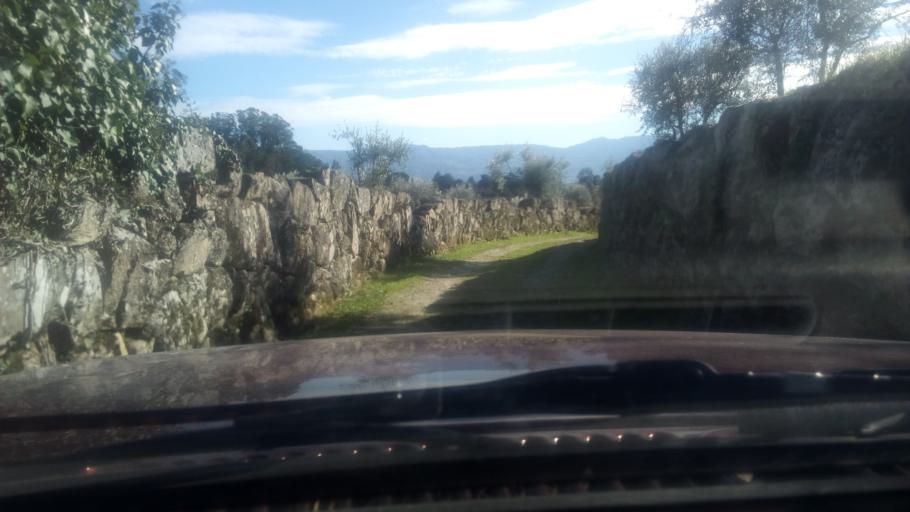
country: PT
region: Guarda
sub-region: Fornos de Algodres
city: Fornos de Algodres
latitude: 40.6225
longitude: -7.5319
